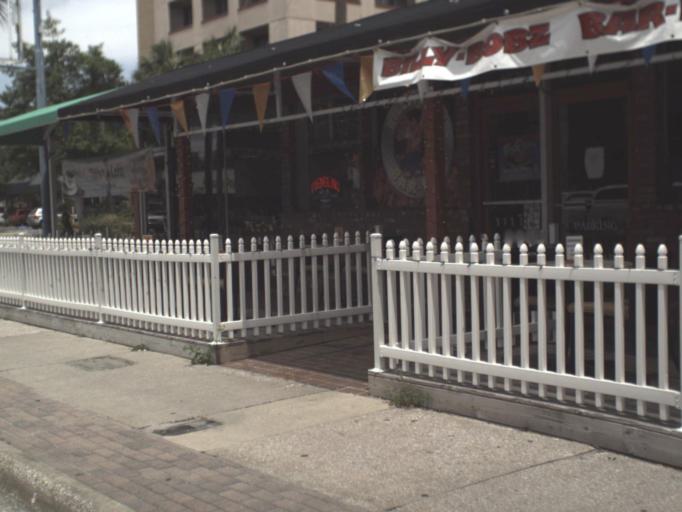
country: US
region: Florida
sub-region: Alachua County
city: Gainesville
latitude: 29.6521
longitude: -82.3380
